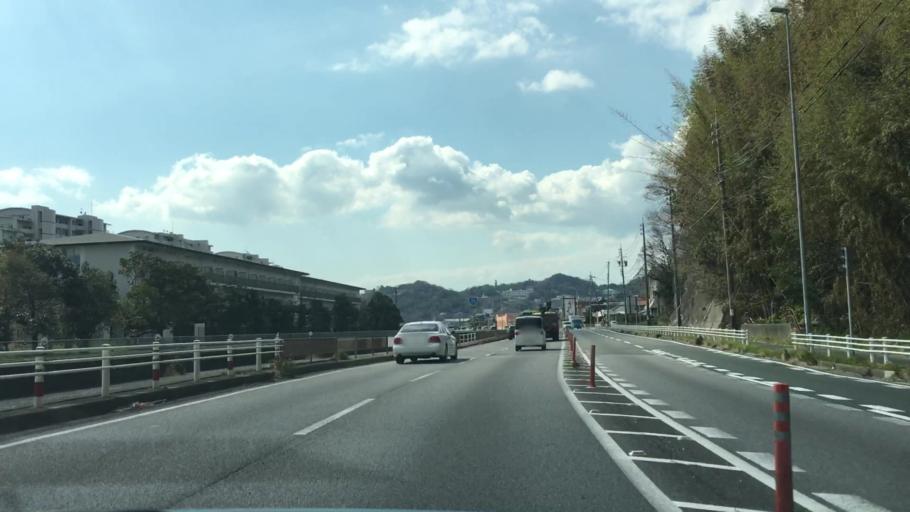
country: JP
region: Aichi
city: Gamagori
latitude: 34.8120
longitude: 137.2822
